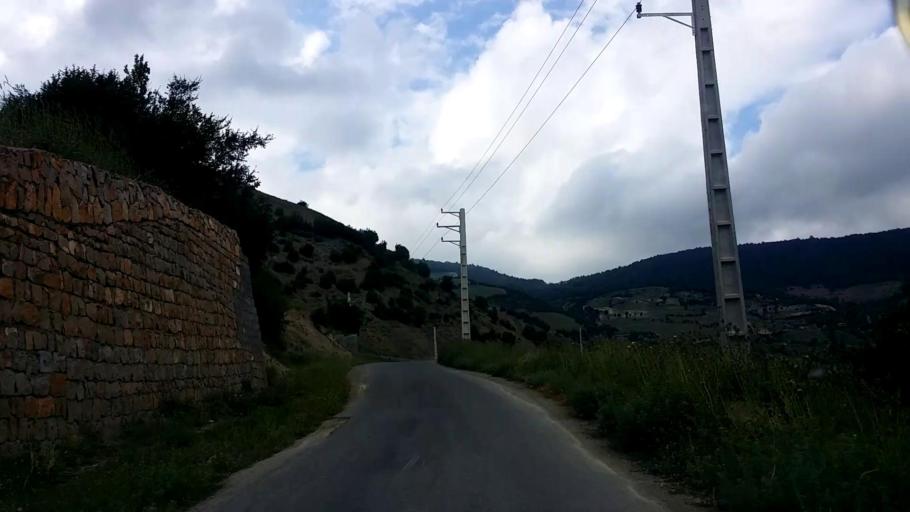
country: IR
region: Mazandaran
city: Chalus
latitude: 36.5462
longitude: 51.2711
